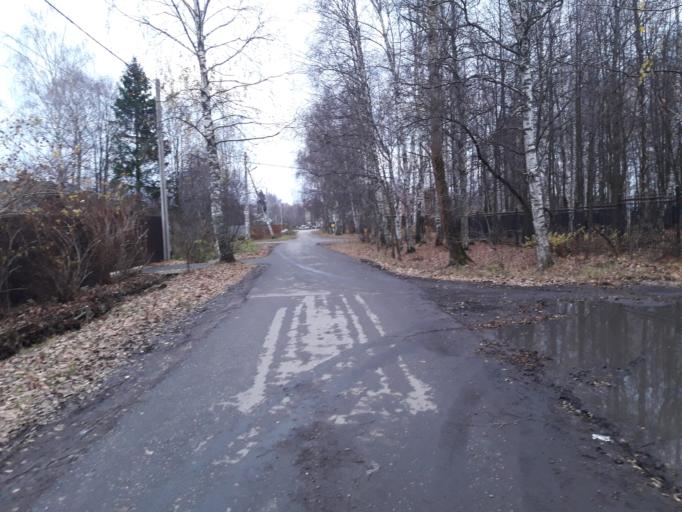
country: RU
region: Moskovskaya
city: Ashukino
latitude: 56.1704
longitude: 37.9433
